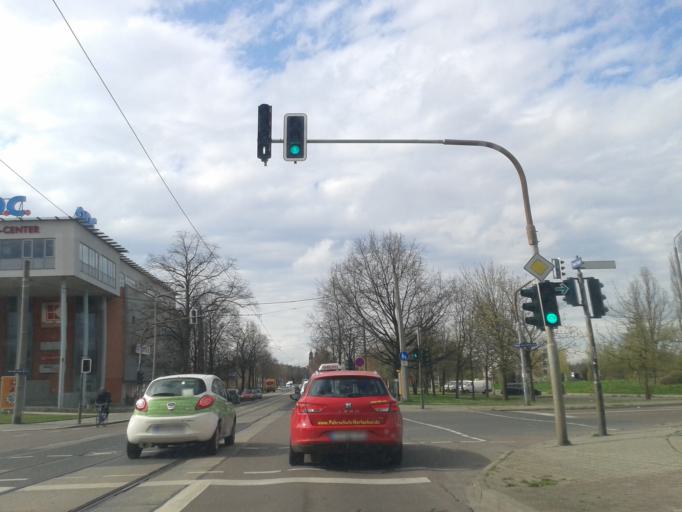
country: DE
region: Saxony
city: Dresden
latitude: 51.0191
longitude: 13.7813
